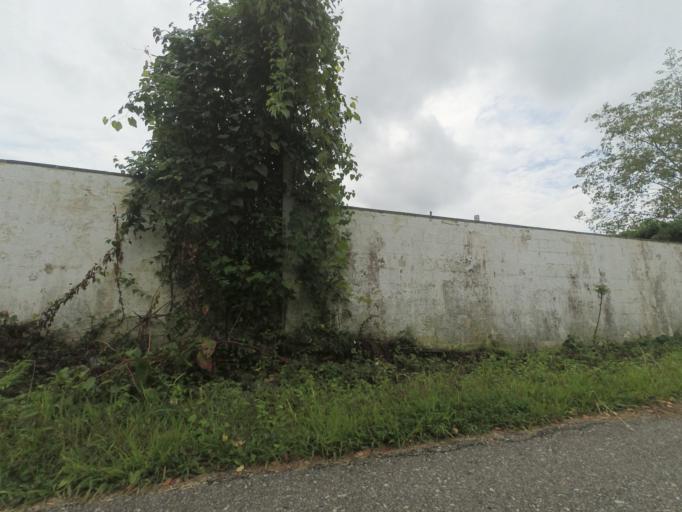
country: US
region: West Virginia
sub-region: Cabell County
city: Huntington
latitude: 38.4258
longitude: -82.4709
